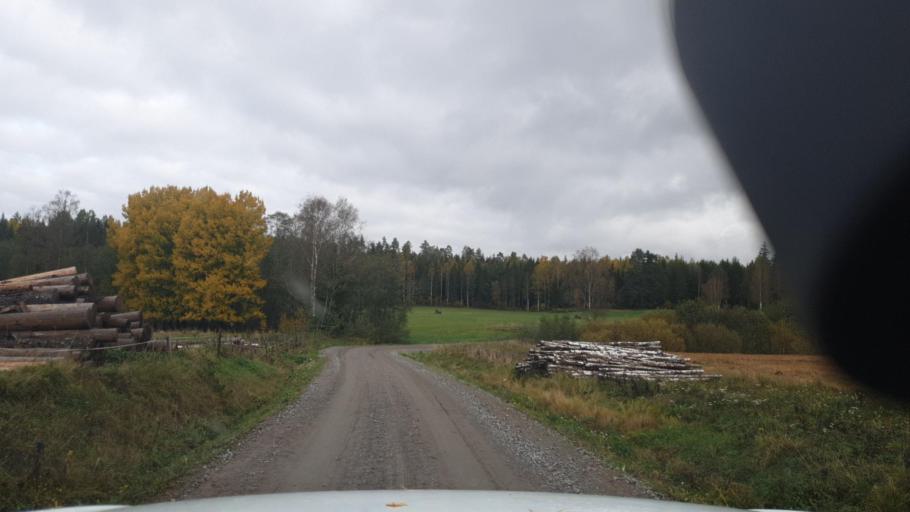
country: SE
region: Vaermland
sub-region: Karlstads Kommun
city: Edsvalla
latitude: 59.4789
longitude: 13.1324
